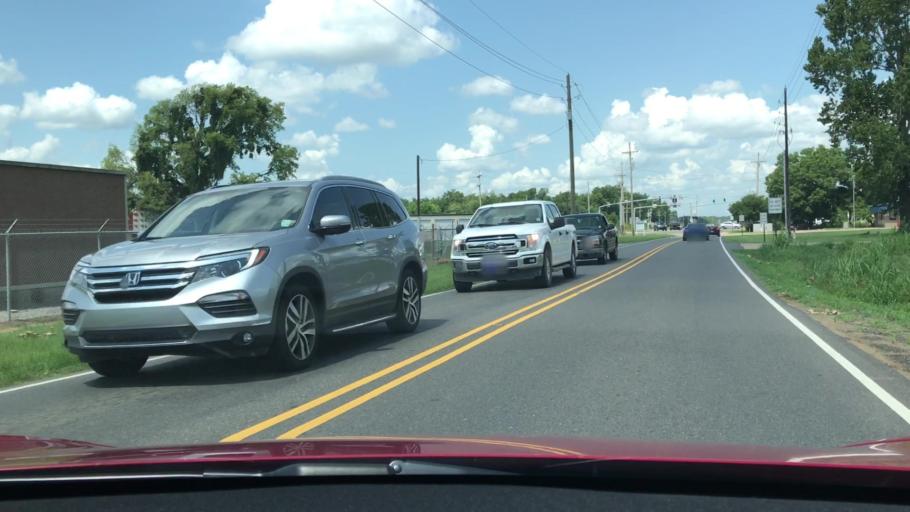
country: US
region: Louisiana
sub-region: Bossier Parish
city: Bossier City
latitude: 32.4009
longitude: -93.6913
